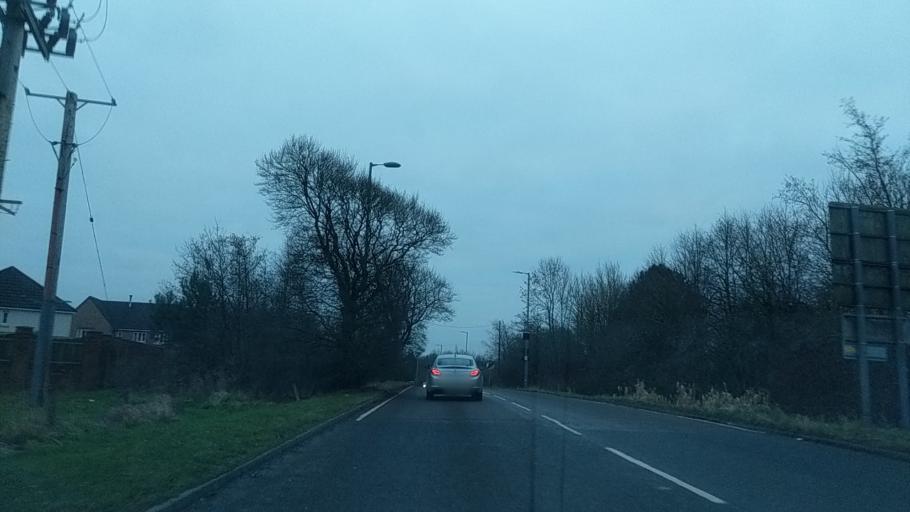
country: GB
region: Scotland
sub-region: South Lanarkshire
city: East Kilbride
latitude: 55.7422
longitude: -4.1578
